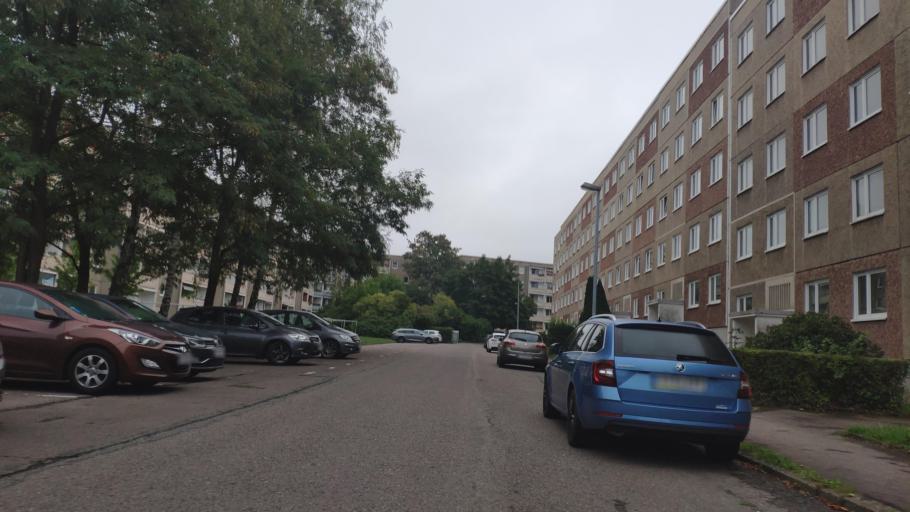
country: DE
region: Saxony
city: Hilbersdorf
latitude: 50.8337
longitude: 12.9682
